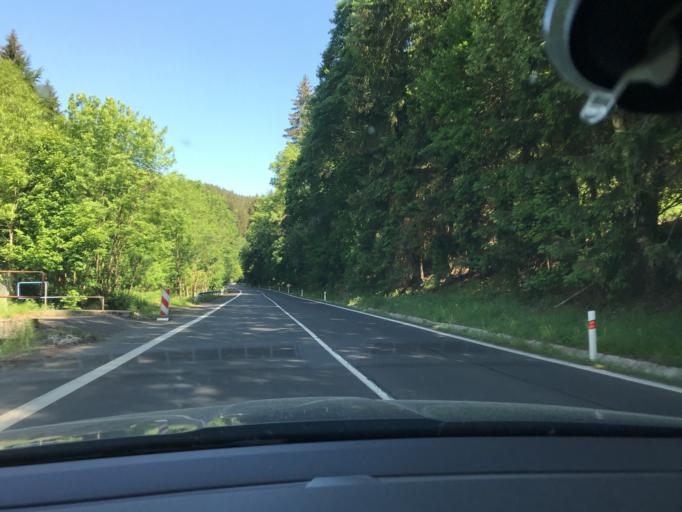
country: CZ
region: Karlovarsky
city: Jachymov
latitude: 50.3483
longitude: 12.9333
